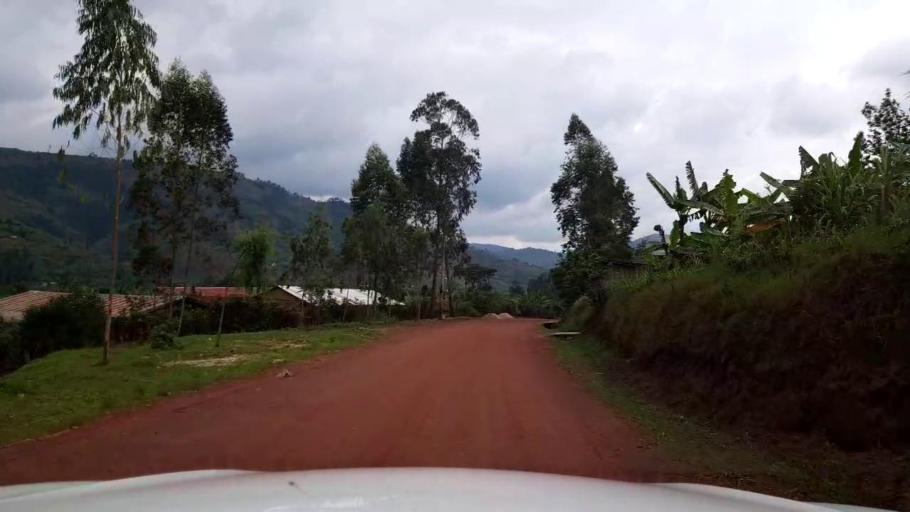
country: RW
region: Northern Province
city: Musanze
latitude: -1.6643
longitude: 29.8021
